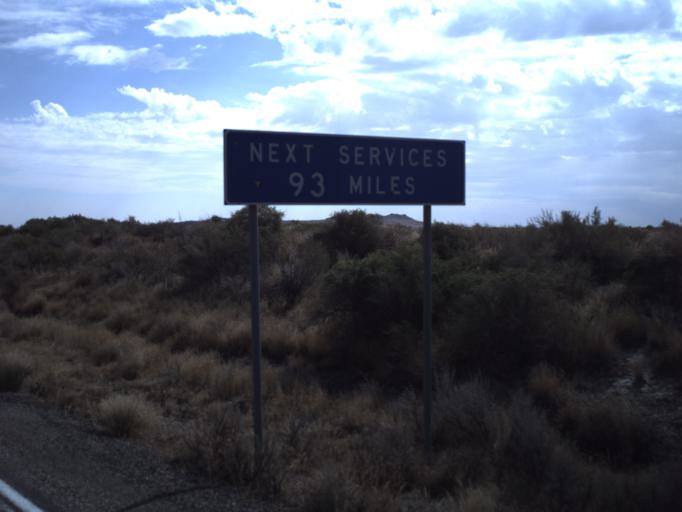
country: US
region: Nevada
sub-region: Elko County
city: West Wendover
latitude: 41.3684
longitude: -114.0397
